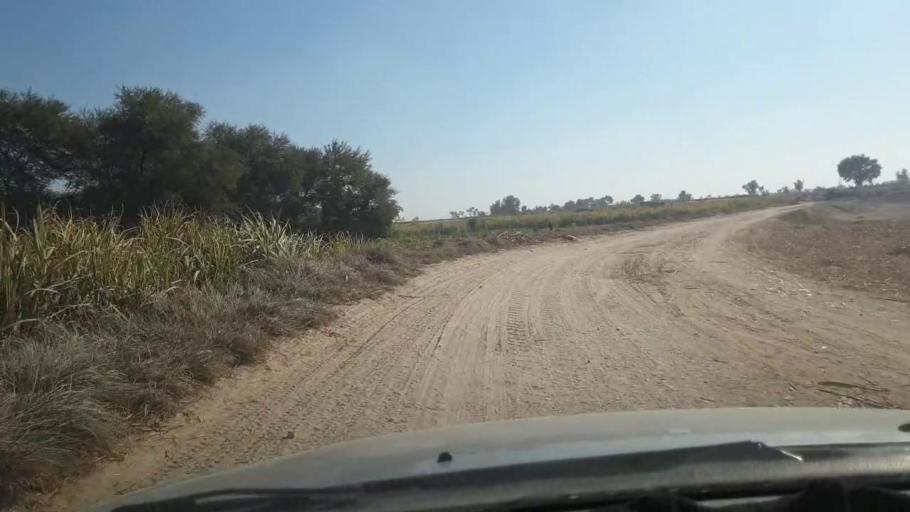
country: PK
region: Sindh
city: Ghotki
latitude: 28.0179
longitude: 69.2242
